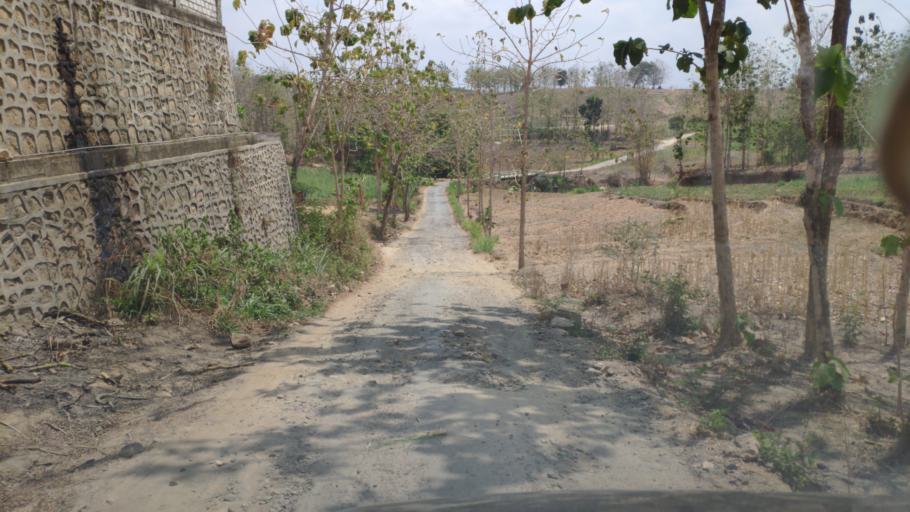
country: ID
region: Central Java
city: Kedungbacin
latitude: -6.8638
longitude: 111.2294
